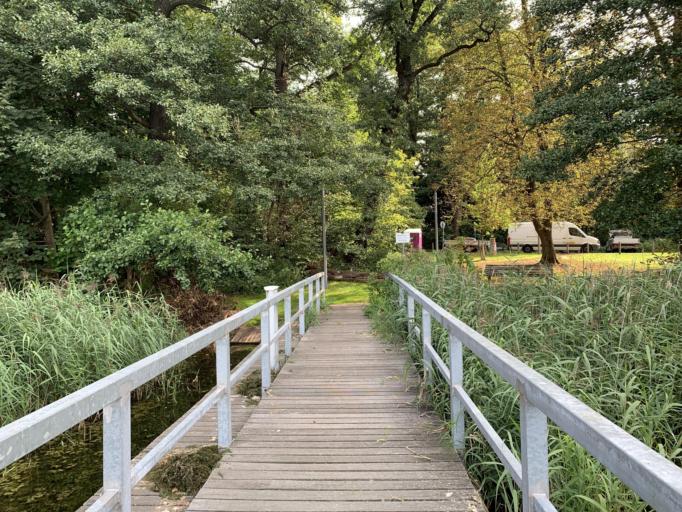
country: DE
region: Brandenburg
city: Grunheide
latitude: 52.4488
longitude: 13.8670
